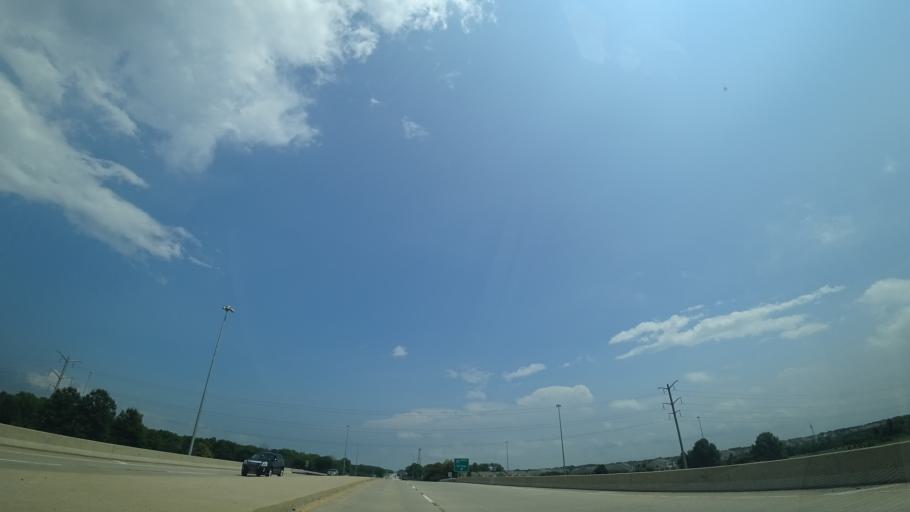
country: US
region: Illinois
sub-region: Cook County
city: Matteson
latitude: 41.5280
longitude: -87.7431
